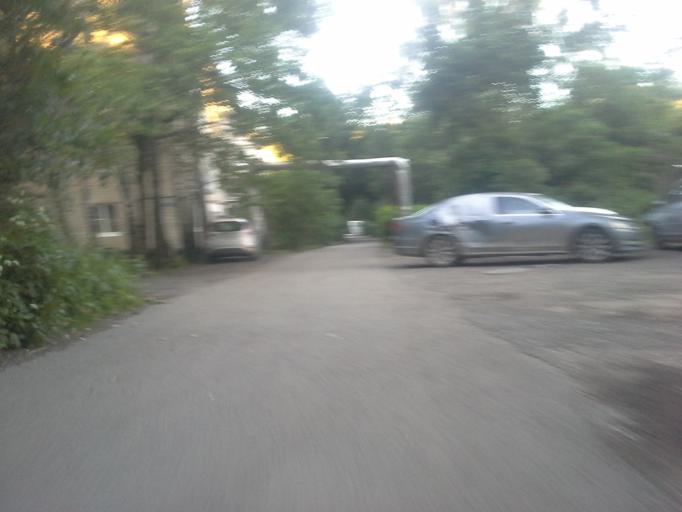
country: RU
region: Moskovskaya
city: Skolkovo
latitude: 55.6620
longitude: 37.3692
